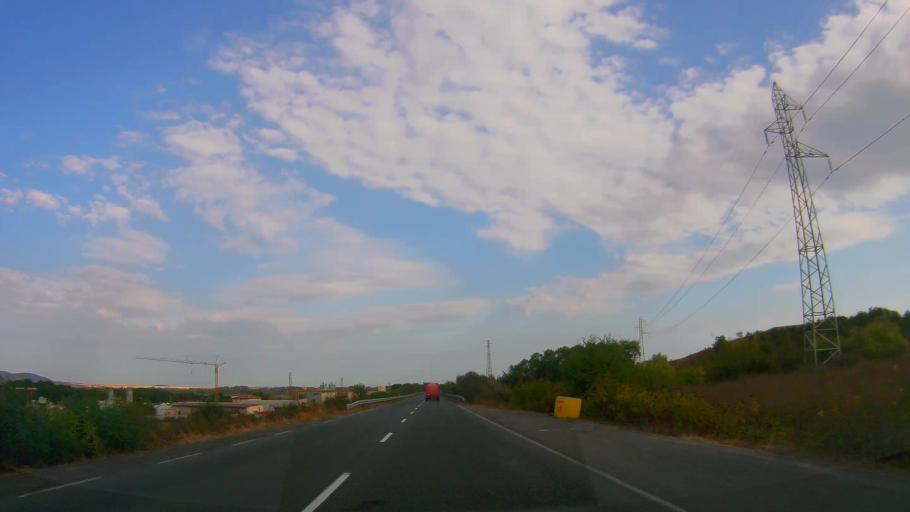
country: BG
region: Burgas
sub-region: Obshtina Sozopol
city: Sozopol
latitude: 42.3929
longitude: 27.6763
